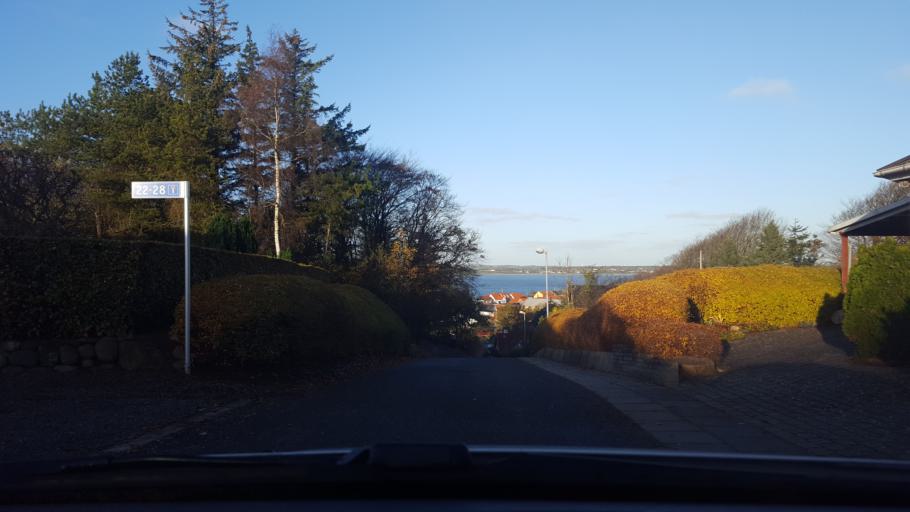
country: DK
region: North Denmark
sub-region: Morso Kommune
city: Nykobing Mors
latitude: 56.7567
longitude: 8.8769
